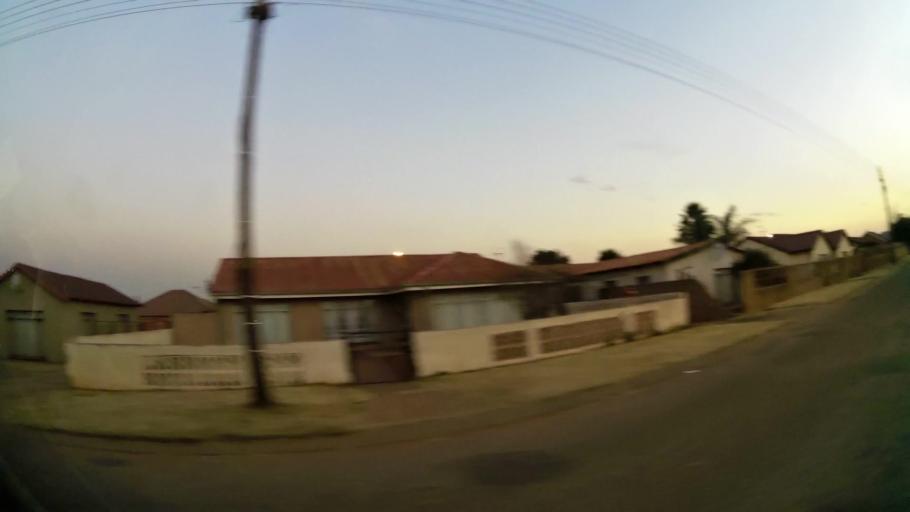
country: ZA
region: Gauteng
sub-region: West Rand District Municipality
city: Randfontein
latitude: -26.2062
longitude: 27.7107
